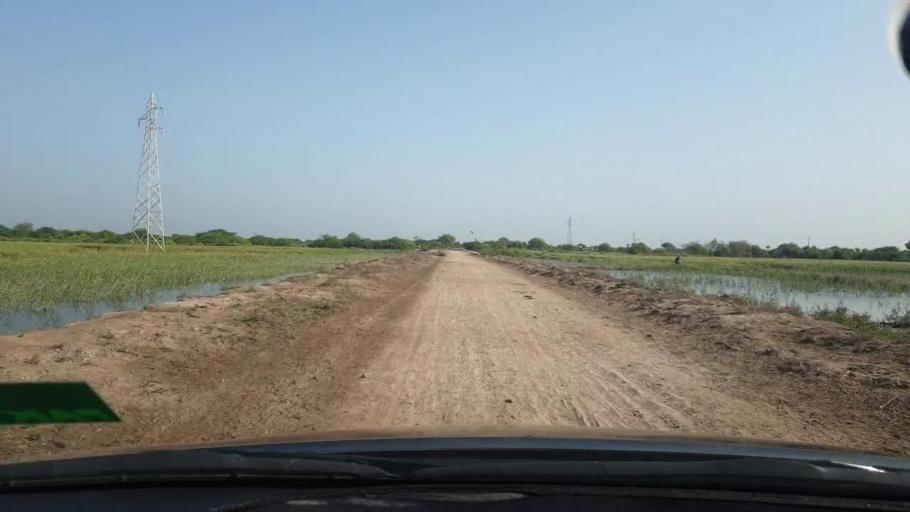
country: PK
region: Sindh
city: Tando Bago
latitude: 24.7176
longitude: 68.9528
